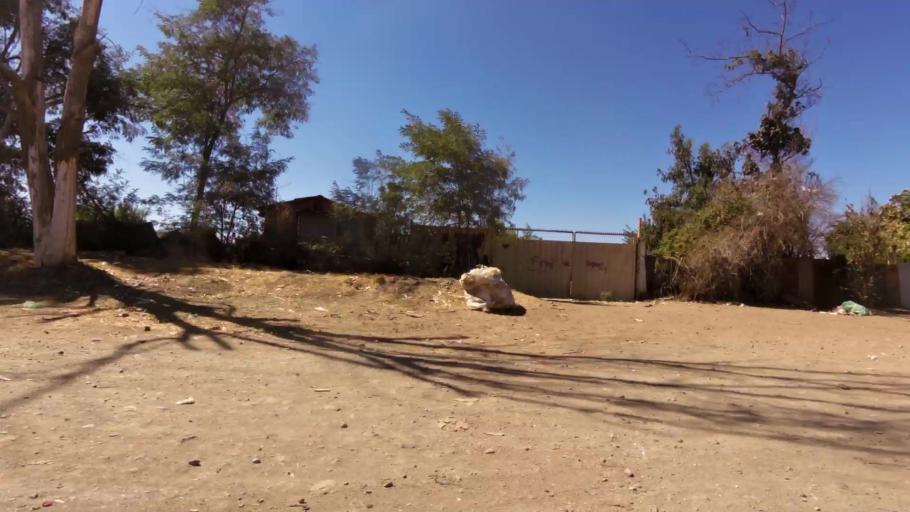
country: CL
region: O'Higgins
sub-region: Provincia de Cachapoal
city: Rancagua
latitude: -34.1677
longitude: -70.7052
